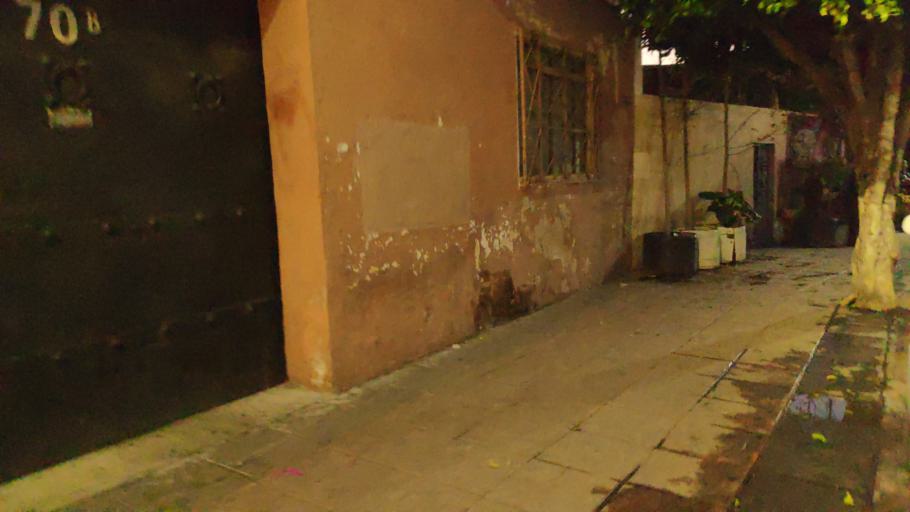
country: MX
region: Queretaro
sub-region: Queretaro
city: Santiago de Queretaro
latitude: 20.5910
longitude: -100.3825
